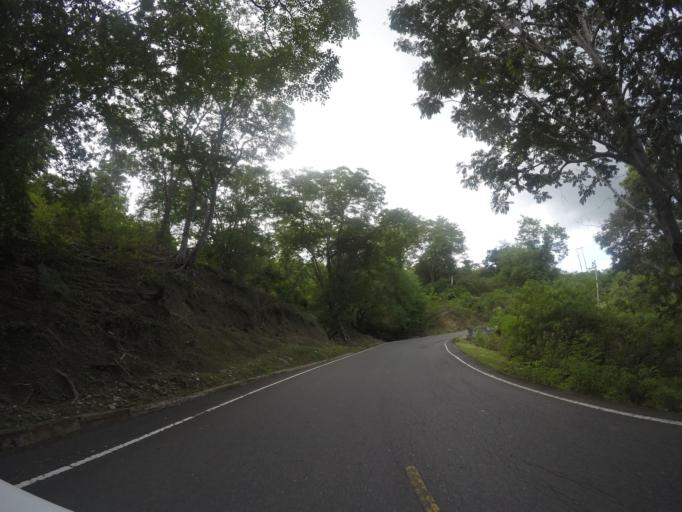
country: TL
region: Bobonaro
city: Maliana
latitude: -8.9526
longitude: 125.0872
